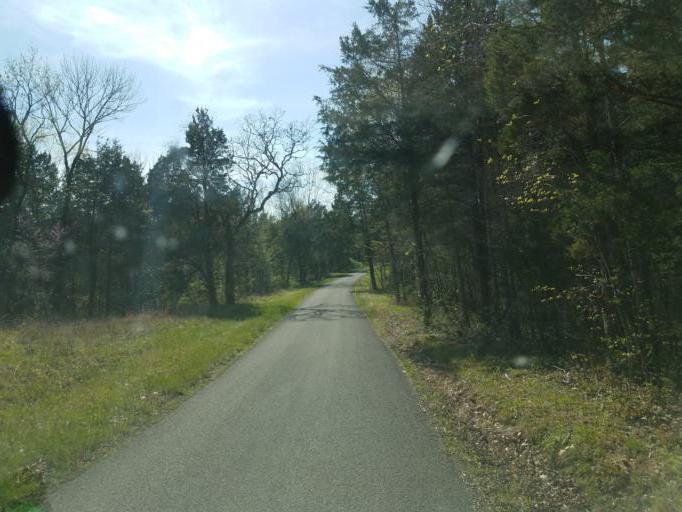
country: US
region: Kentucky
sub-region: Barren County
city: Cave City
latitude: 37.1411
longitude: -85.9676
